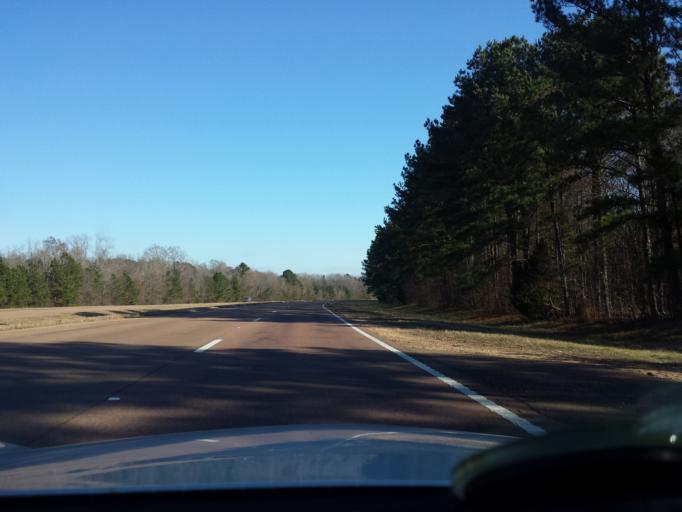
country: US
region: Mississippi
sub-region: Madison County
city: Canton
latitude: 32.5129
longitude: -89.8698
